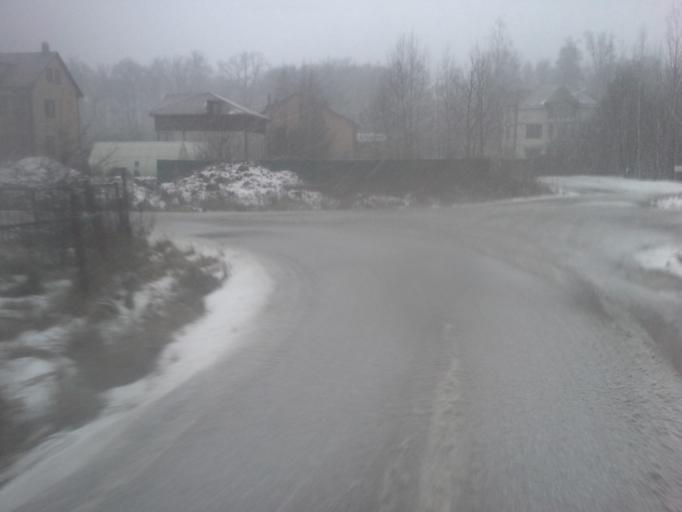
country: RU
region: Moskovskaya
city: Kommunarka
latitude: 55.5888
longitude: 37.4874
